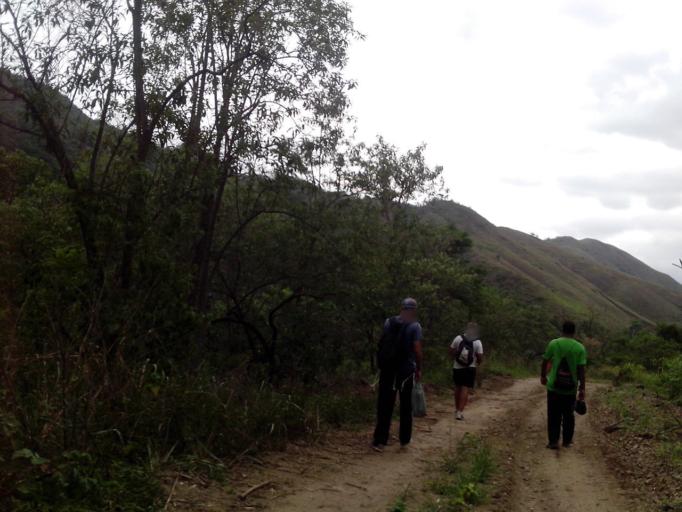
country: BR
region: Rio de Janeiro
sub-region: Miguel Pereira
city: Miguel Pereira
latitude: -22.5082
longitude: -43.5131
